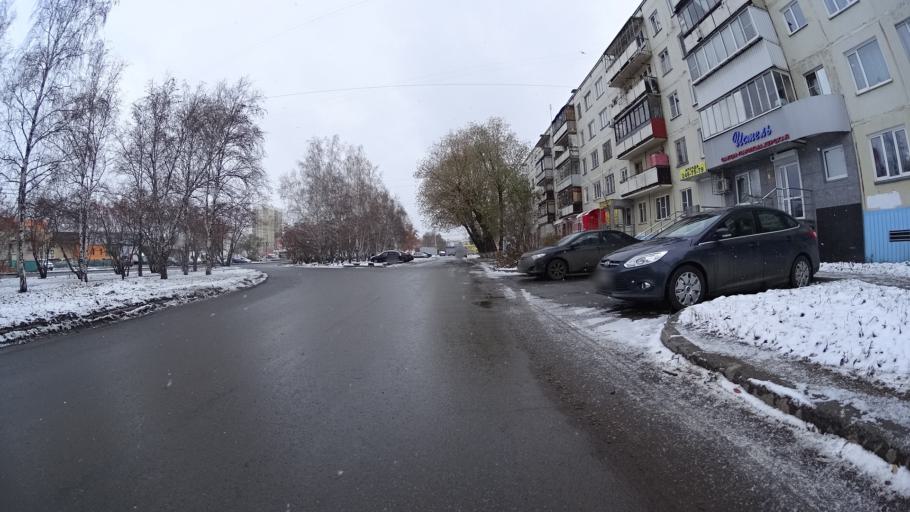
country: RU
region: Chelyabinsk
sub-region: Gorod Chelyabinsk
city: Chelyabinsk
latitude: 55.1928
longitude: 61.3220
